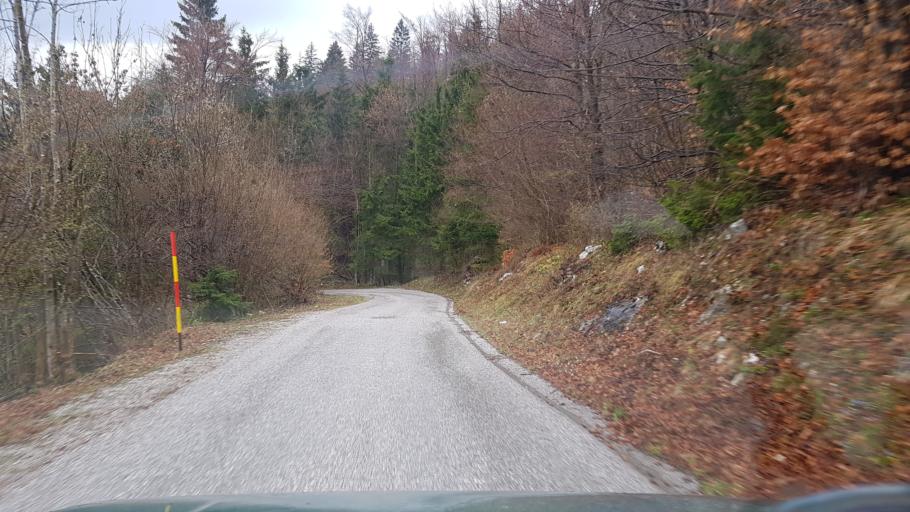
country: SI
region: Cerkno
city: Cerkno
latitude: 46.1347
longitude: 13.8786
